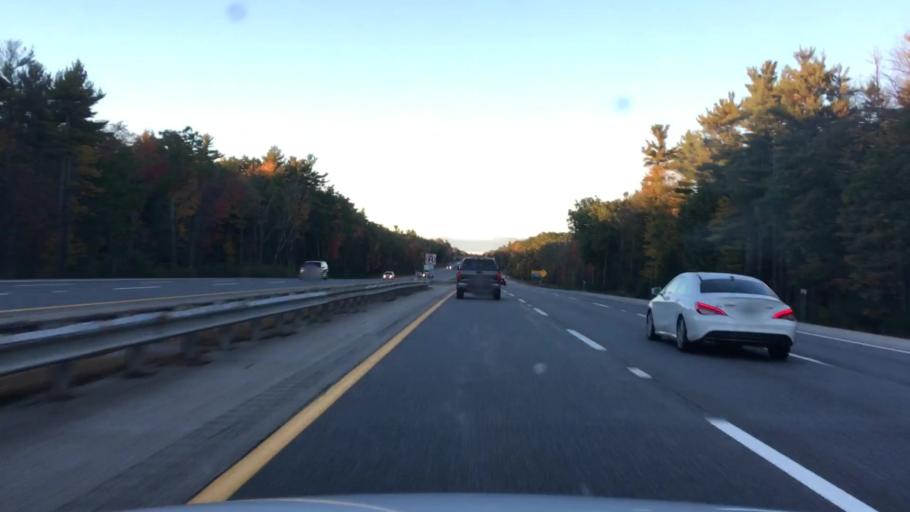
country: US
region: Maine
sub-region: York County
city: Ogunquit
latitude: 43.2848
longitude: -70.6171
